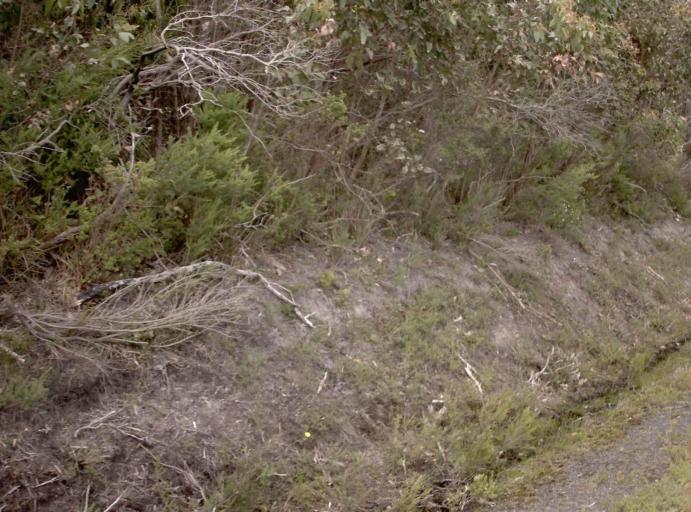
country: AU
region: Victoria
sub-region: Latrobe
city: Morwell
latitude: -39.0168
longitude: 146.3026
